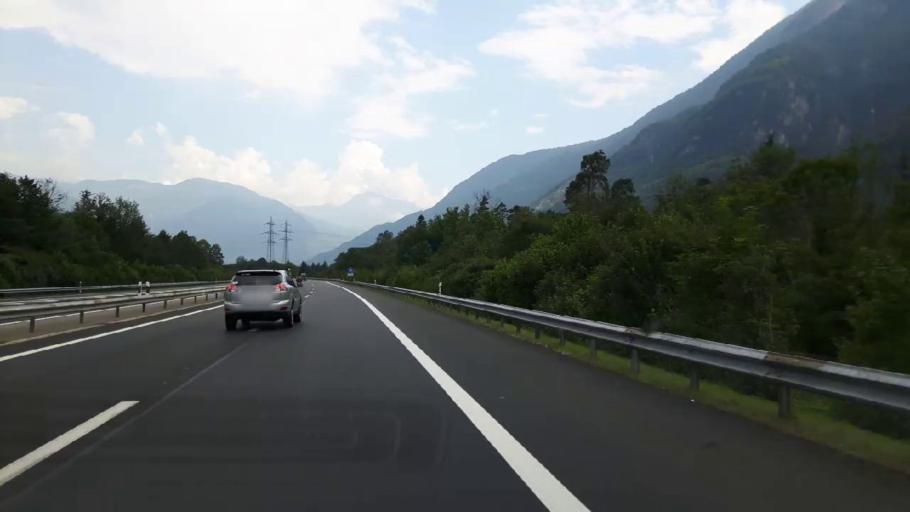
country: CH
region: Ticino
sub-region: Riviera District
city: Lodrino
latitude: 46.2780
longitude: 8.9952
